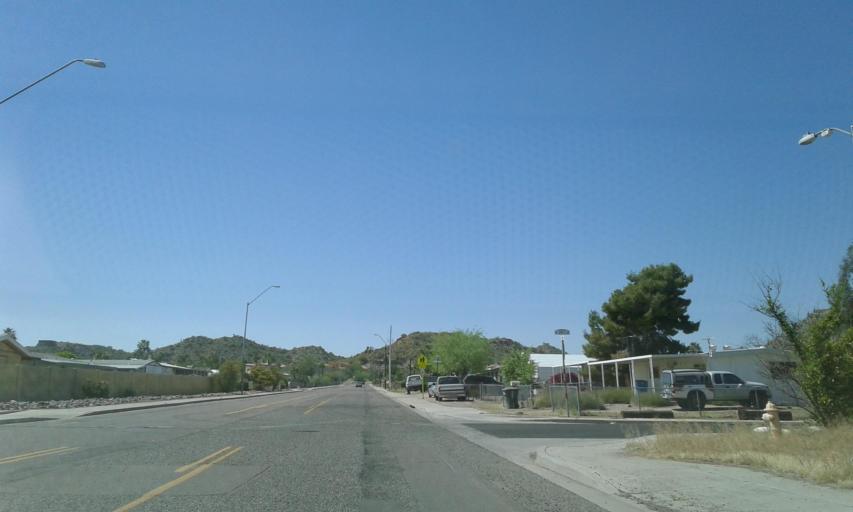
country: US
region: Arizona
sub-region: Maricopa County
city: Paradise Valley
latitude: 33.6624
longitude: -112.0246
